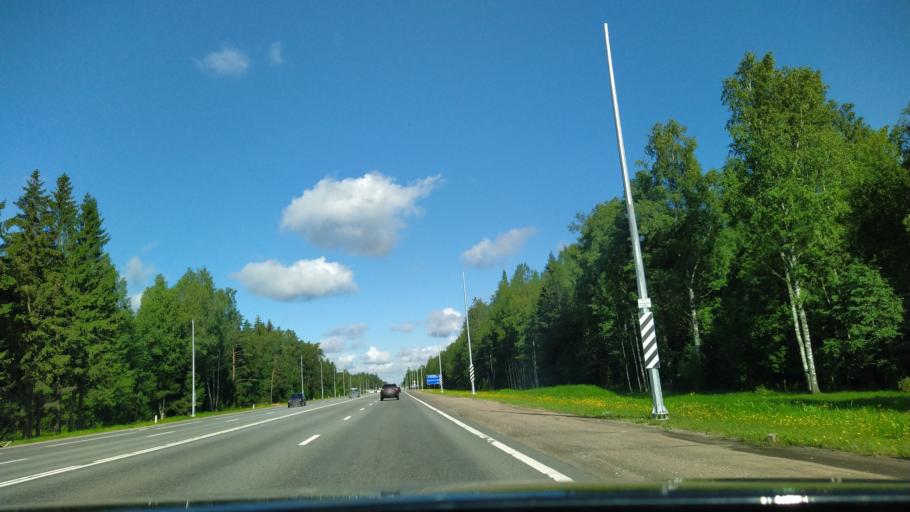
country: RU
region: Leningrad
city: Ul'yanovka
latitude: 59.5805
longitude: 30.8054
